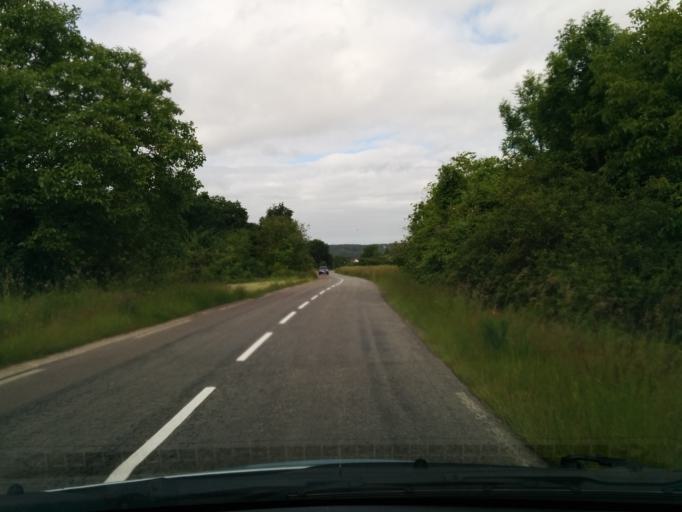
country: FR
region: Ile-de-France
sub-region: Departement des Yvelines
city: Rosny-sur-Seine
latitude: 49.0118
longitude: 1.6481
